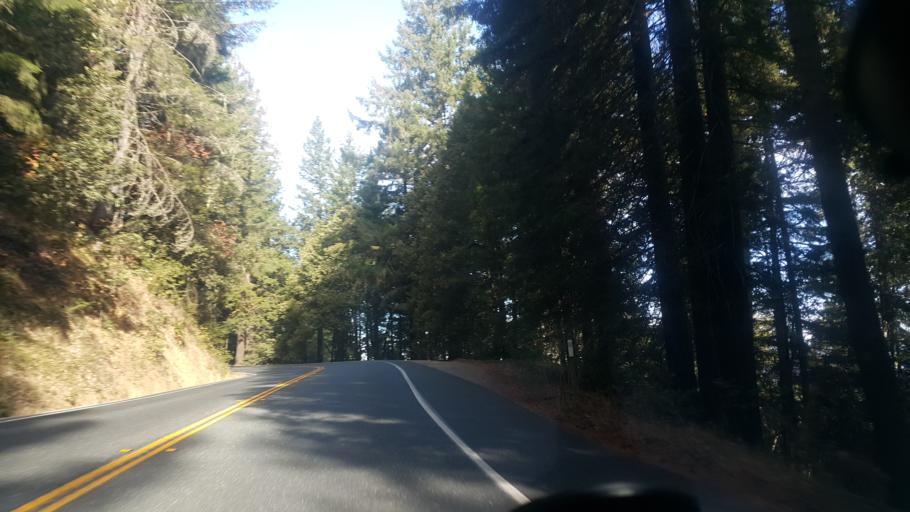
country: US
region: California
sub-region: Mendocino County
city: Brooktrails
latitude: 39.3928
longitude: -123.4622
